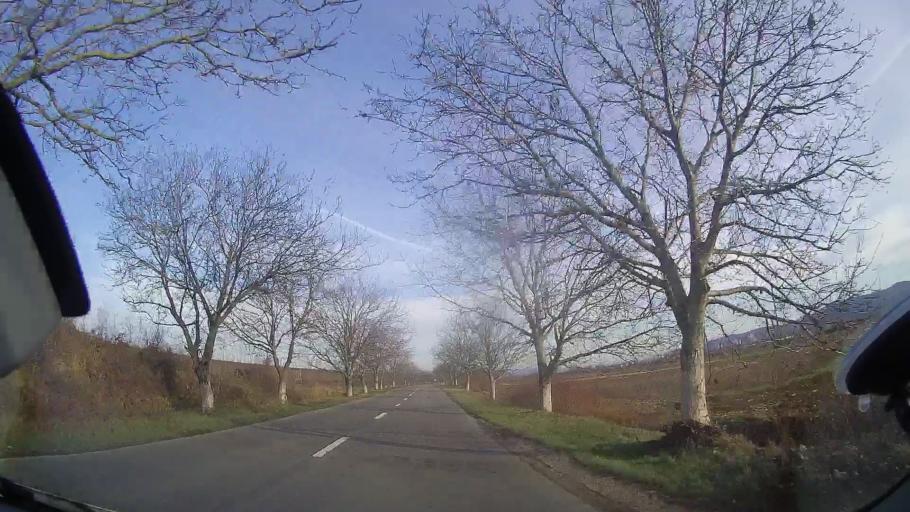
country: RO
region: Bihor
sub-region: Comuna Tetchea
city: Hotar
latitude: 47.0518
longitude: 22.3033
